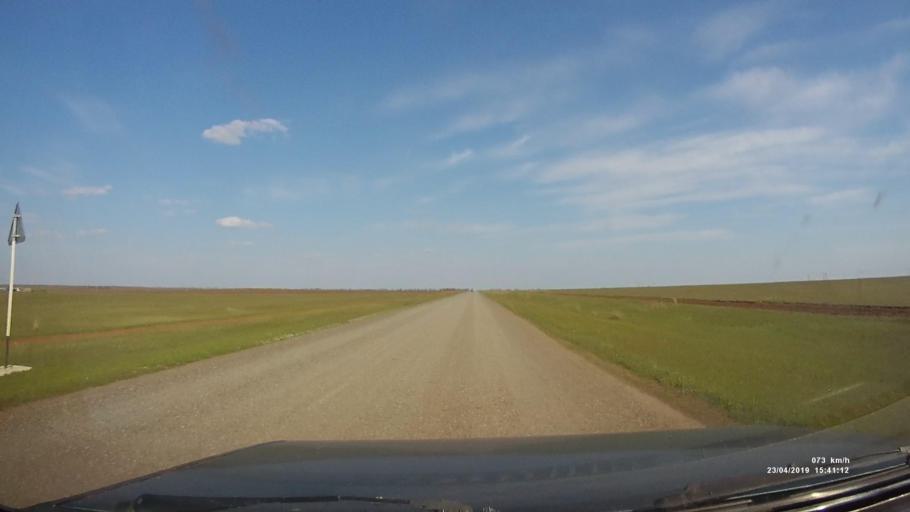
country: RU
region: Rostov
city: Remontnoye
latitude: 46.5524
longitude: 43.0480
